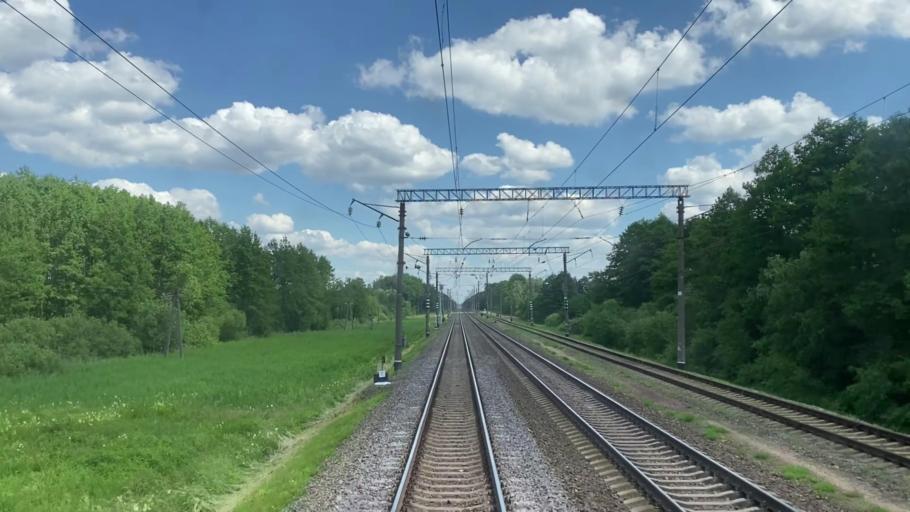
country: BY
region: Brest
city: Byaroza
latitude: 52.5385
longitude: 24.9261
